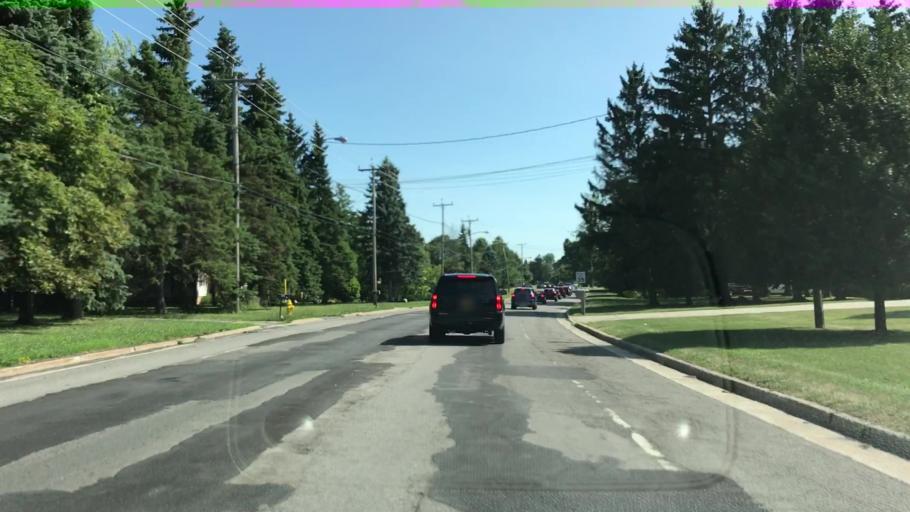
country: US
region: New York
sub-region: Erie County
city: Depew
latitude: 42.8867
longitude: -78.7087
